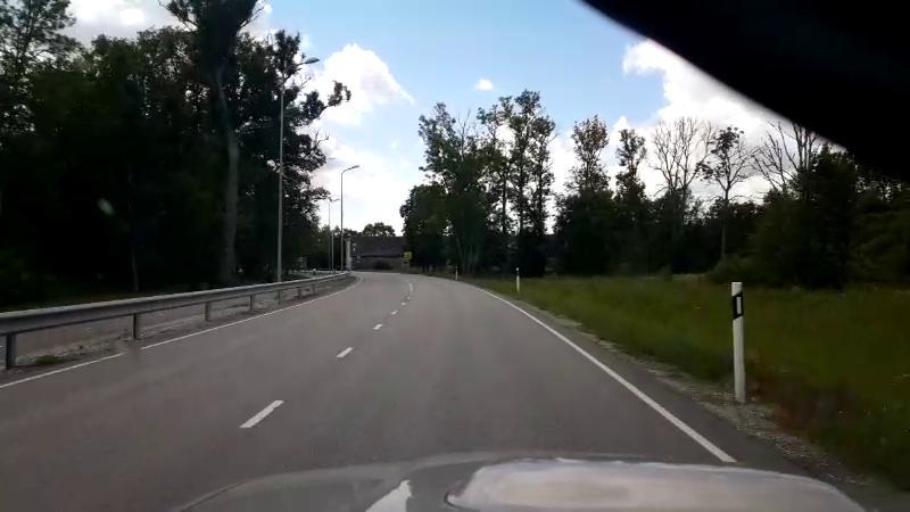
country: EE
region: Jaervamaa
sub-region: Jaerva-Jaani vald
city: Jarva-Jaani
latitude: 59.0310
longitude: 25.7039
